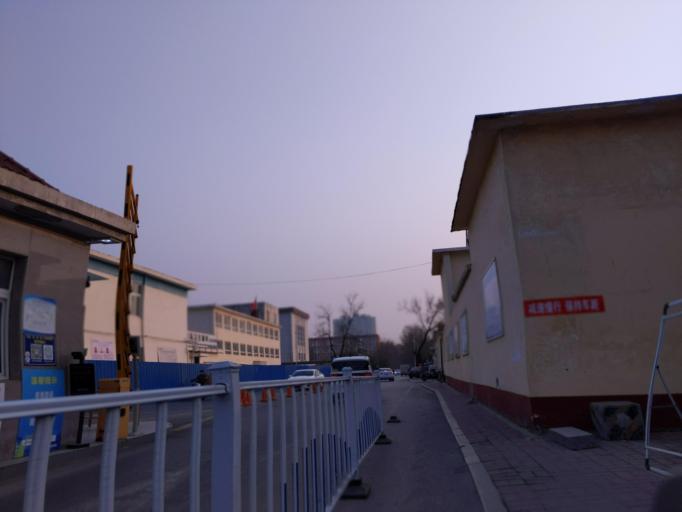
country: CN
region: Henan Sheng
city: Zhongyuanlu
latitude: 35.7859
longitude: 115.0638
